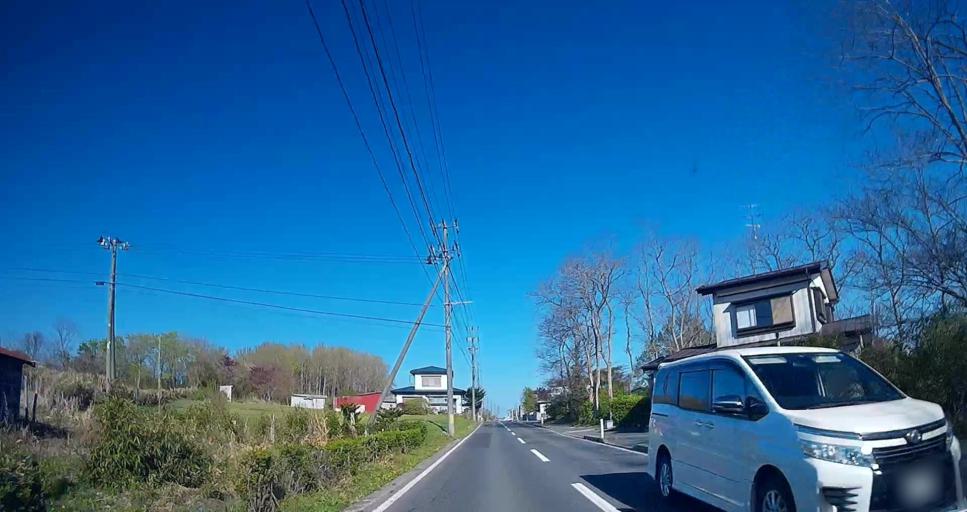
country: JP
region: Aomori
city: Hachinohe
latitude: 40.5207
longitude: 141.5700
